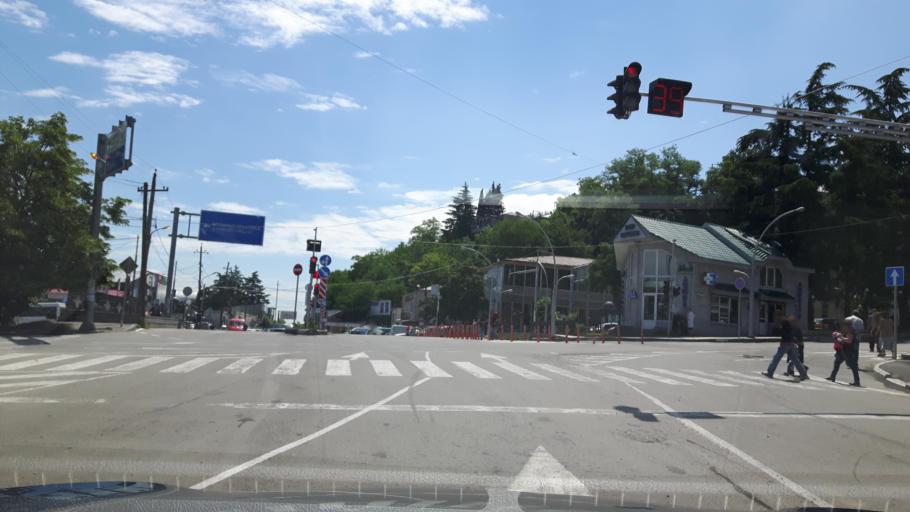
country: GE
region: Kakheti
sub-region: Telavi
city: Telavi
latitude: 41.9224
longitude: 45.4695
